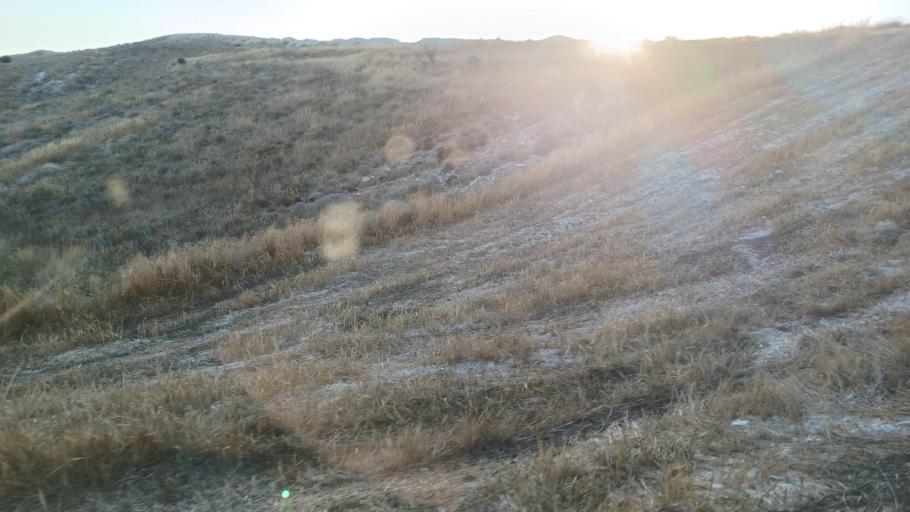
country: CY
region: Larnaka
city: Athienou
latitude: 35.0367
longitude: 33.4988
